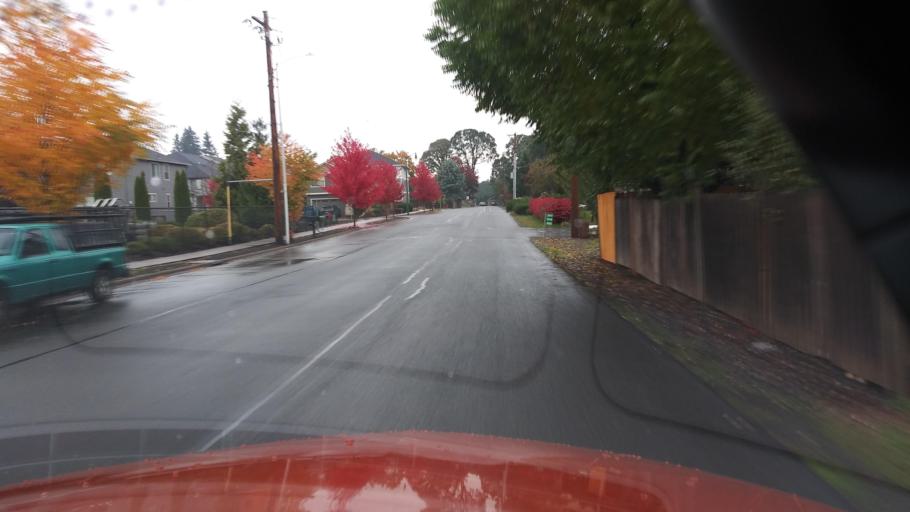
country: US
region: Oregon
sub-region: Washington County
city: Forest Grove
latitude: 45.5255
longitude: -123.0991
